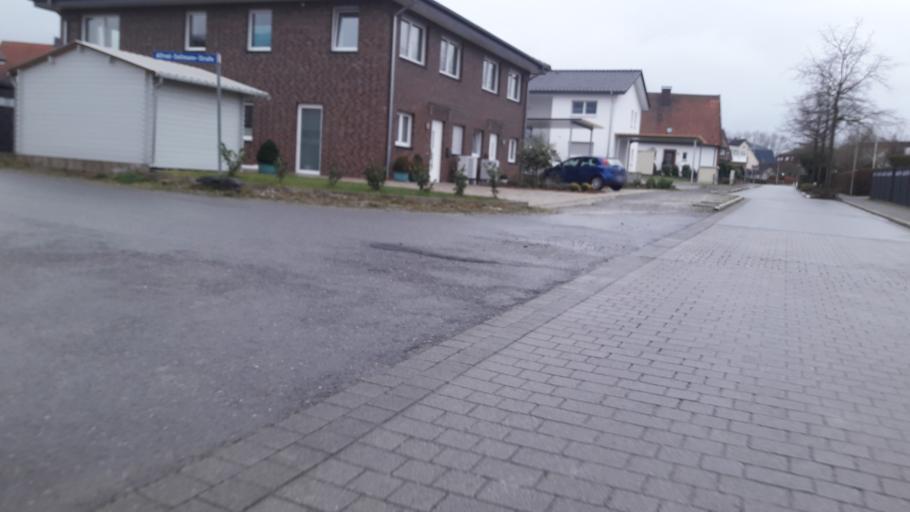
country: DE
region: North Rhine-Westphalia
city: Geseke
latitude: 51.6314
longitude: 8.5041
